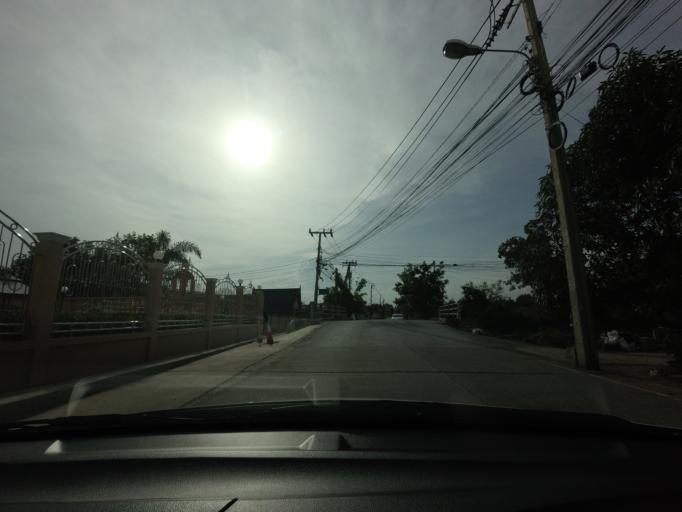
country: TH
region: Bangkok
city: Bang Na
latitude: 13.6491
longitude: 100.6592
